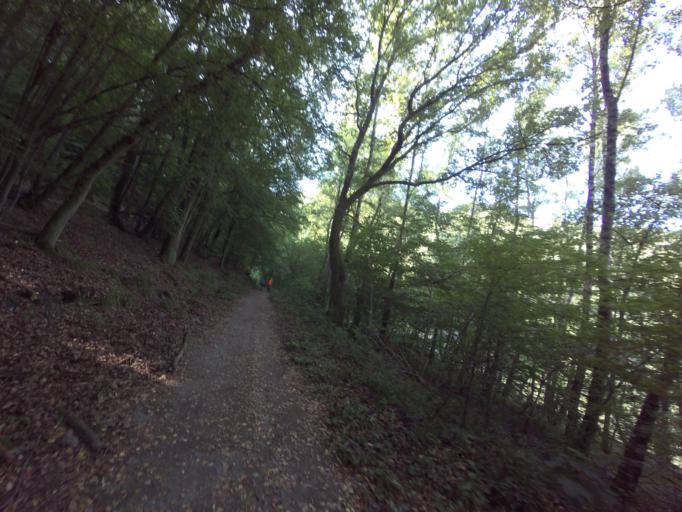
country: DE
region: North Rhine-Westphalia
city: Heimbach
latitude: 50.6014
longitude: 6.4158
